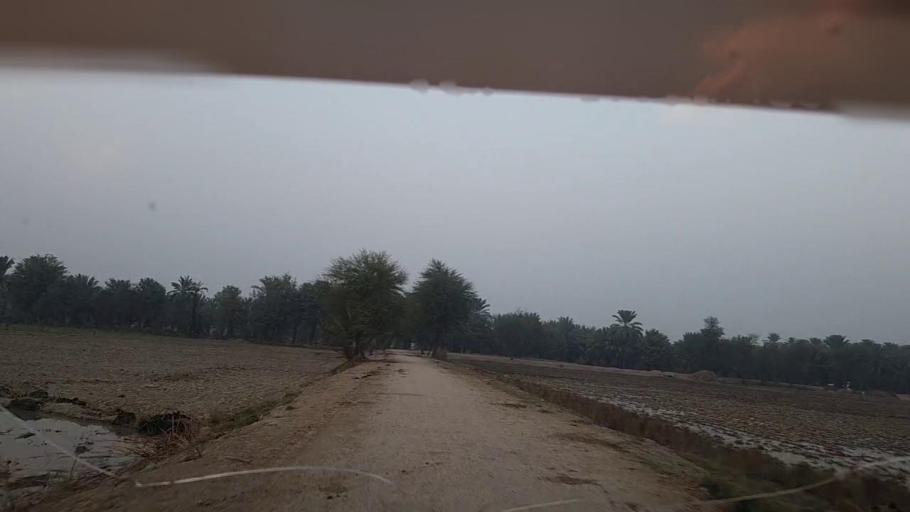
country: PK
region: Sindh
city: Khairpur
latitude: 27.5794
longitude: 68.7359
